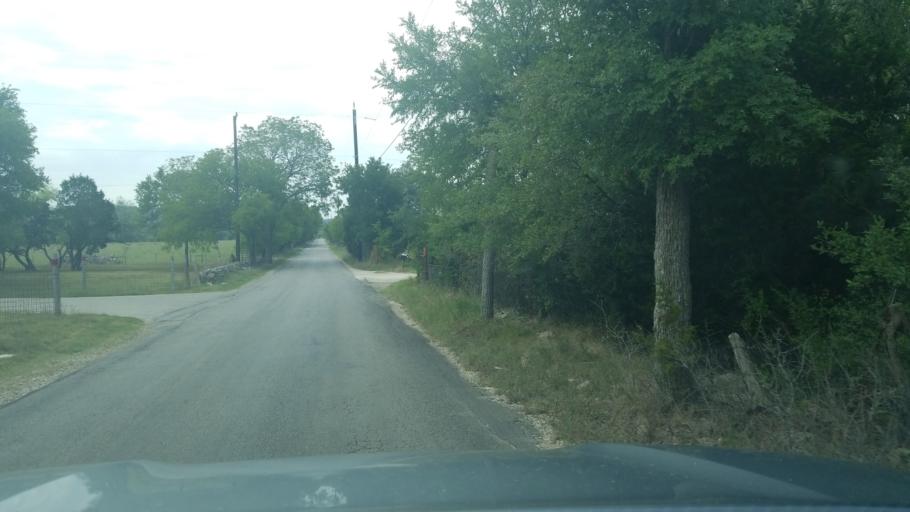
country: US
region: Texas
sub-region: Comal County
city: Bulverde
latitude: 29.7529
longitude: -98.4110
